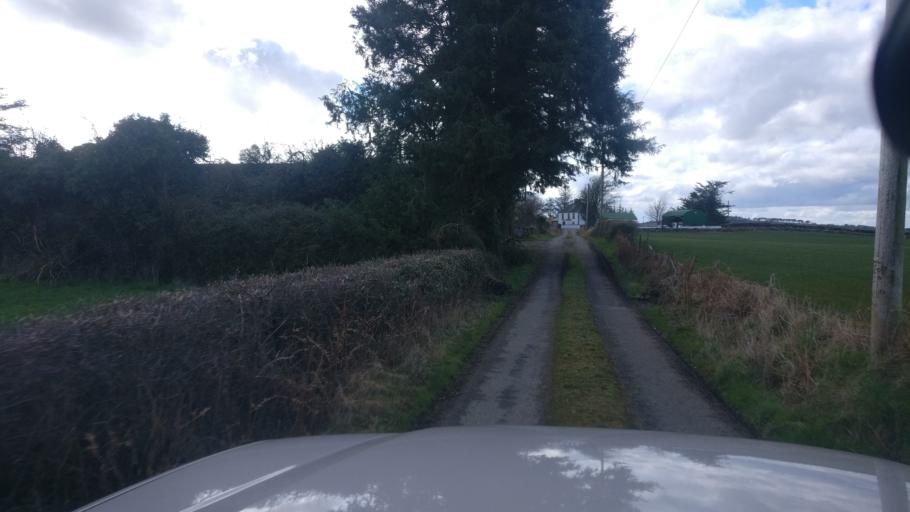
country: IE
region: Connaught
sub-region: County Galway
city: Loughrea
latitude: 53.1828
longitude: -8.4411
